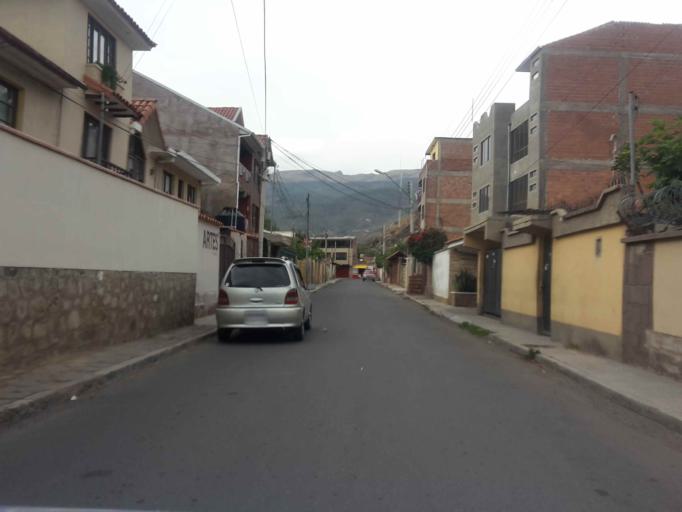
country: BO
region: Cochabamba
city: Cochabamba
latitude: -17.3868
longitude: -66.1421
